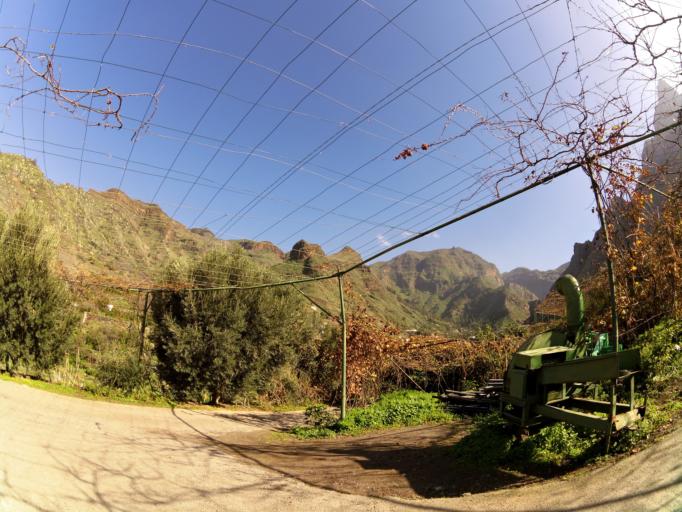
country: ES
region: Canary Islands
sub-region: Provincia de Las Palmas
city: Agaete
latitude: 28.0769
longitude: -15.6704
